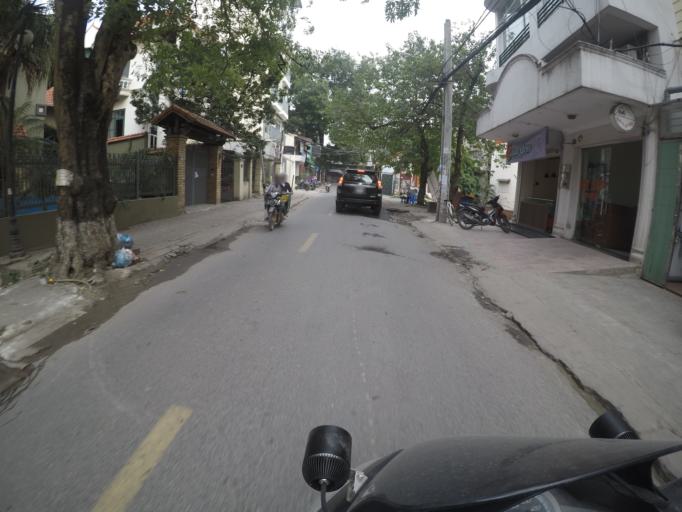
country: VN
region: Ha Noi
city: Tay Ho
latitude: 21.0681
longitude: 105.8254
